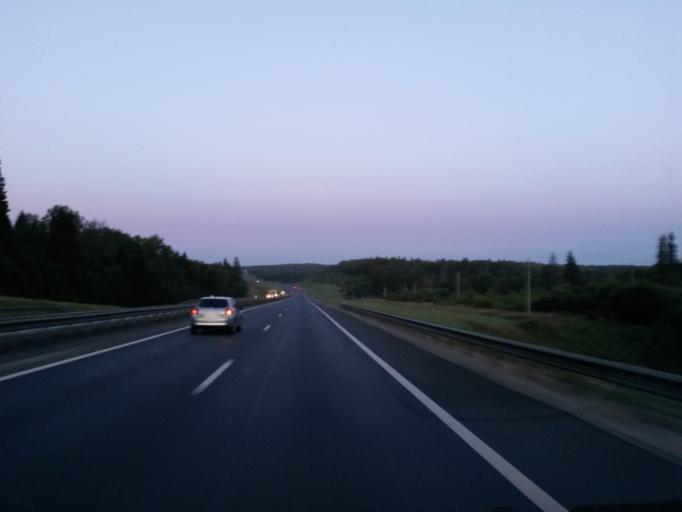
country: RU
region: Vladimir
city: Arsaki
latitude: 56.4865
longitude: 38.4234
